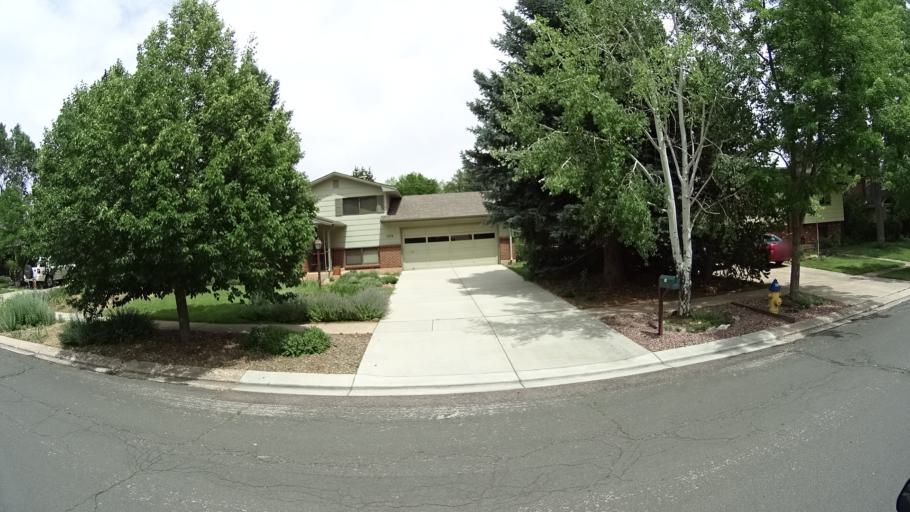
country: US
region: Colorado
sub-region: El Paso County
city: Manitou Springs
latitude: 38.8698
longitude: -104.8709
